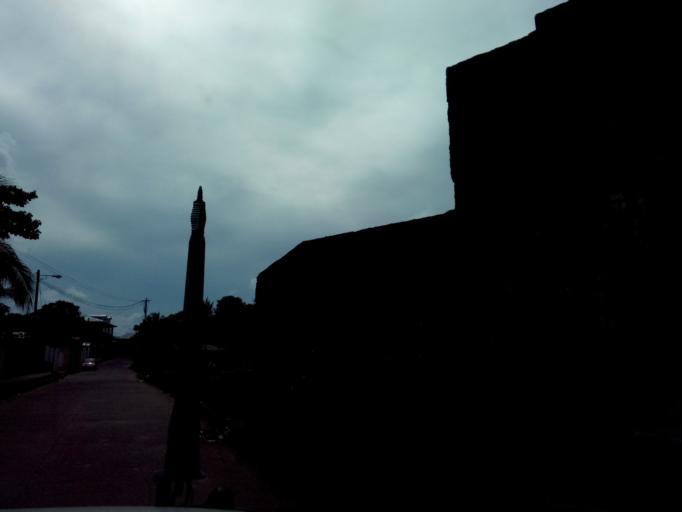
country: NI
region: Atlantico Sur
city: Bluefields
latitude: 12.0240
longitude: -83.7621
